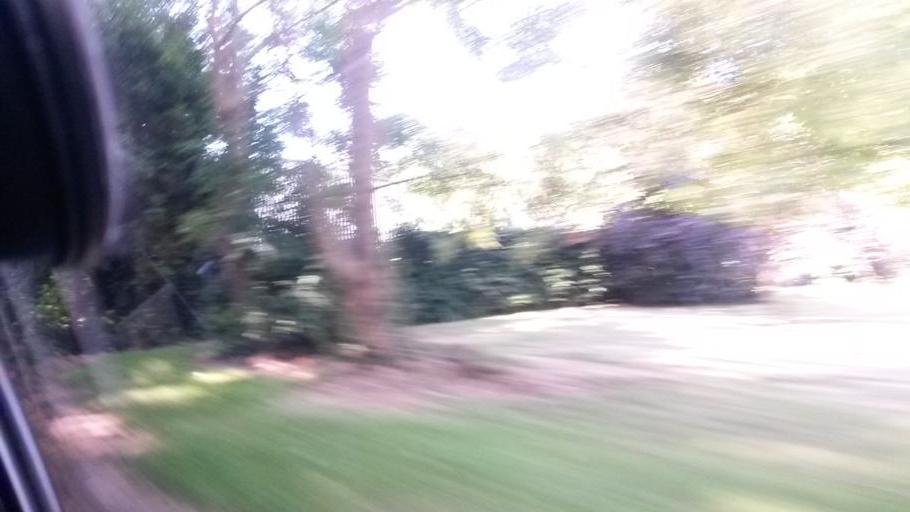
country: IE
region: Leinster
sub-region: An Mhi
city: Stamullin
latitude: 53.5697
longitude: -6.2809
